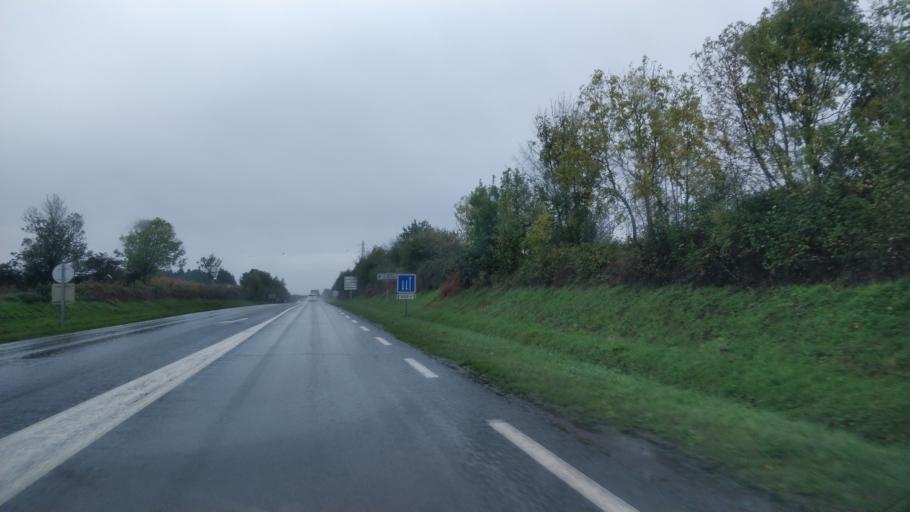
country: FR
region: Lower Normandy
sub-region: Departement de la Manche
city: Saint-Planchers
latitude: 48.8423
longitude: -1.5402
